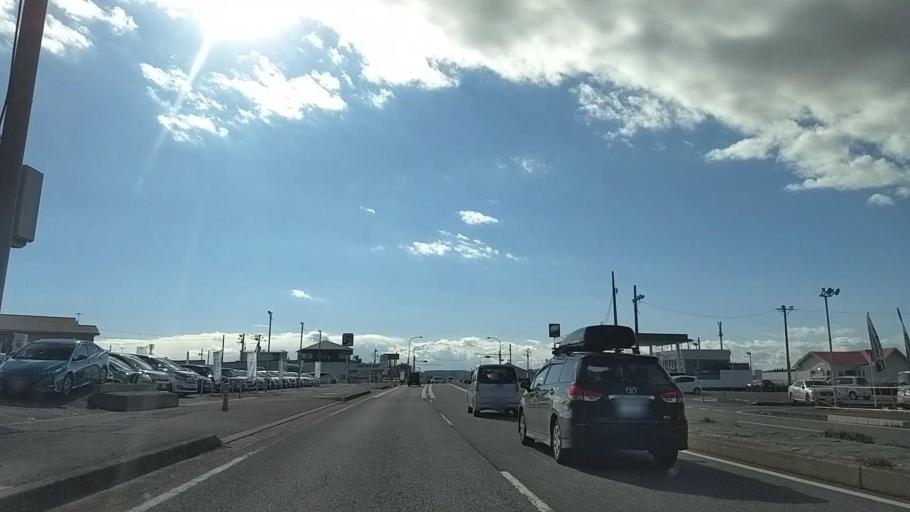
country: JP
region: Chiba
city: Tateyama
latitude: 35.0171
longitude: 139.8718
